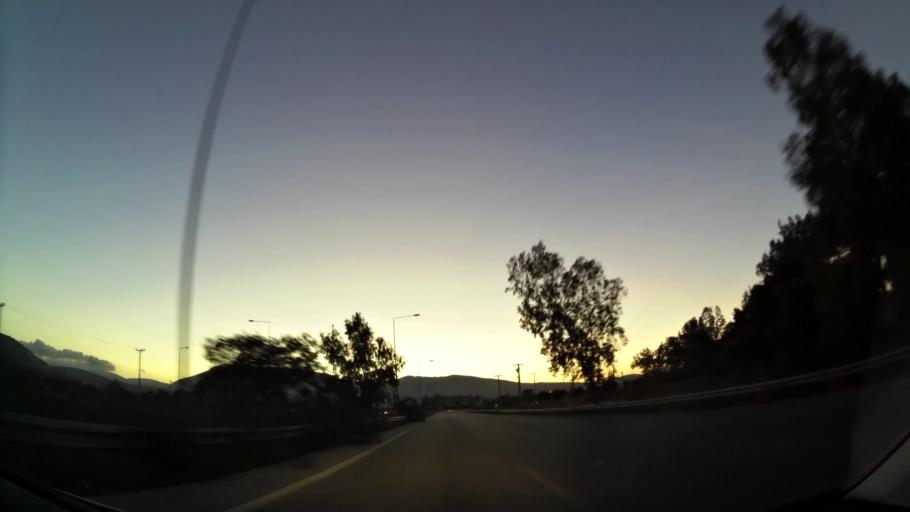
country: GR
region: Attica
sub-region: Nomarchia Anatolikis Attikis
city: Argithea
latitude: 37.9929
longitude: 23.8974
